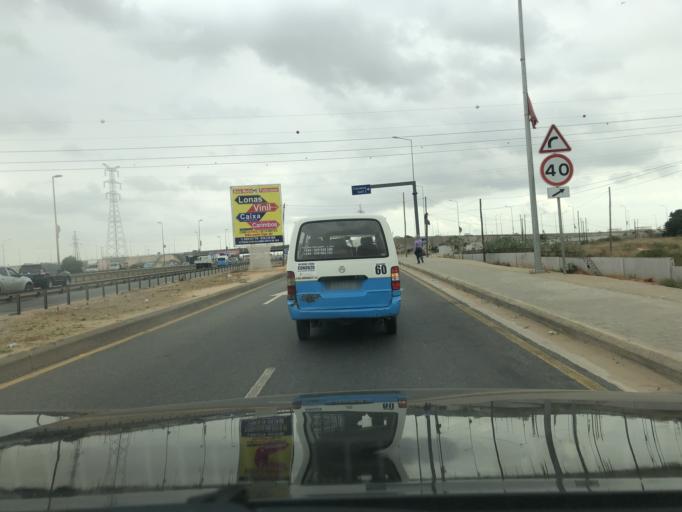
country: AO
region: Luanda
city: Luanda
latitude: -8.9729
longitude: 13.2573
